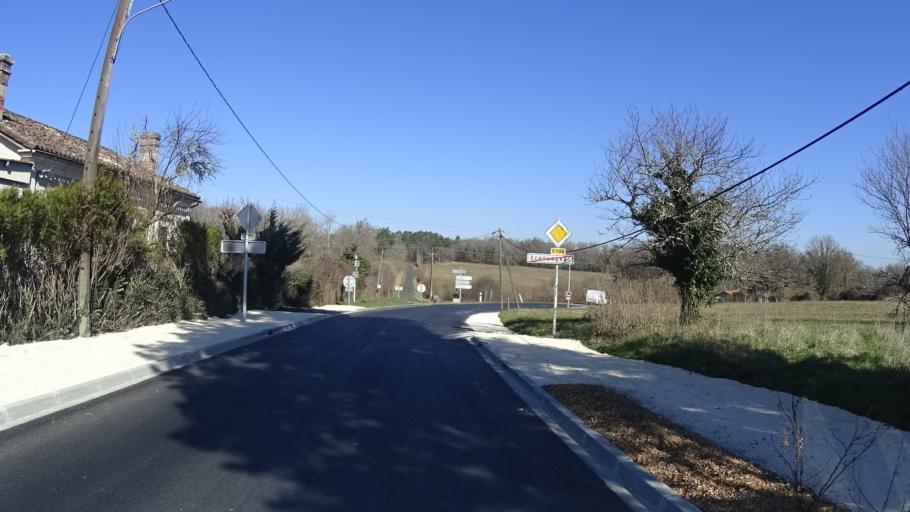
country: FR
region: Aquitaine
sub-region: Departement de la Dordogne
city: Saint-Aulaye
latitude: 45.1275
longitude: 0.2299
